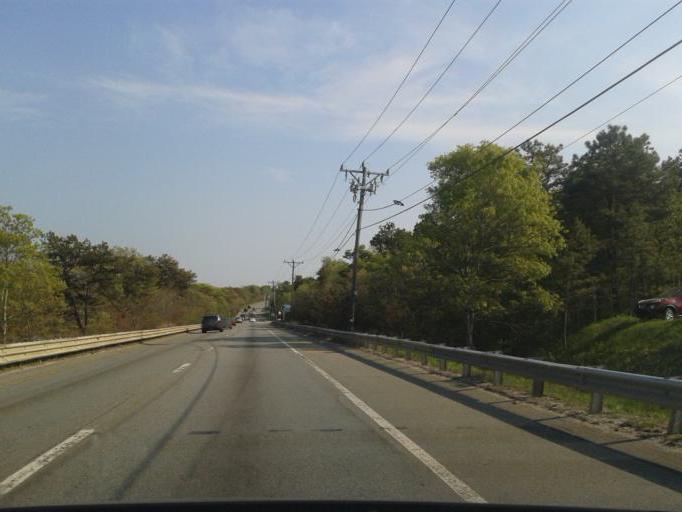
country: US
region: Massachusetts
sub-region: Barnstable County
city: Bourne
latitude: 41.7385
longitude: -70.5855
